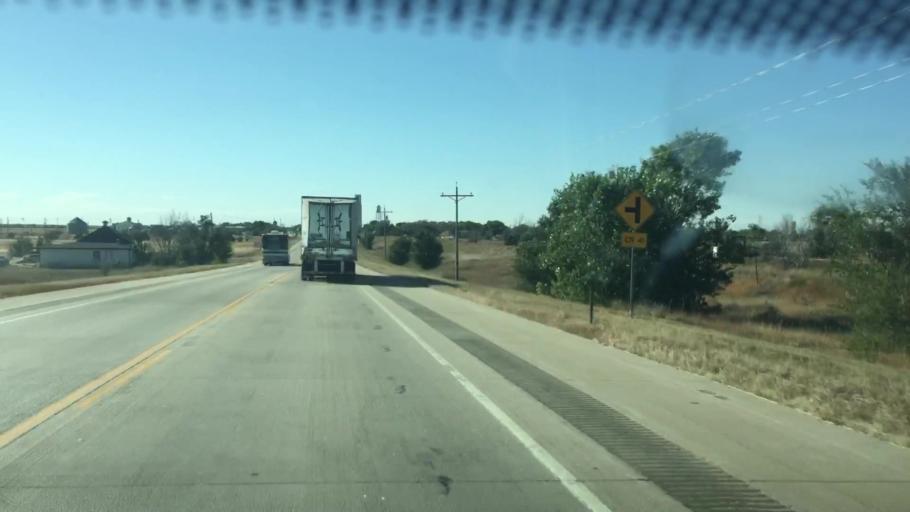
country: US
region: Colorado
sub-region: Kiowa County
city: Eads
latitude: 38.4766
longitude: -102.7657
